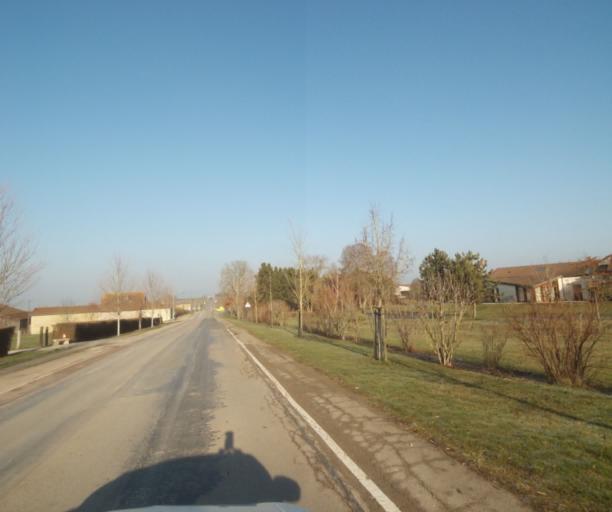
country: FR
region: Champagne-Ardenne
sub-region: Departement de la Haute-Marne
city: Montier-en-Der
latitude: 48.4858
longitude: 4.7604
